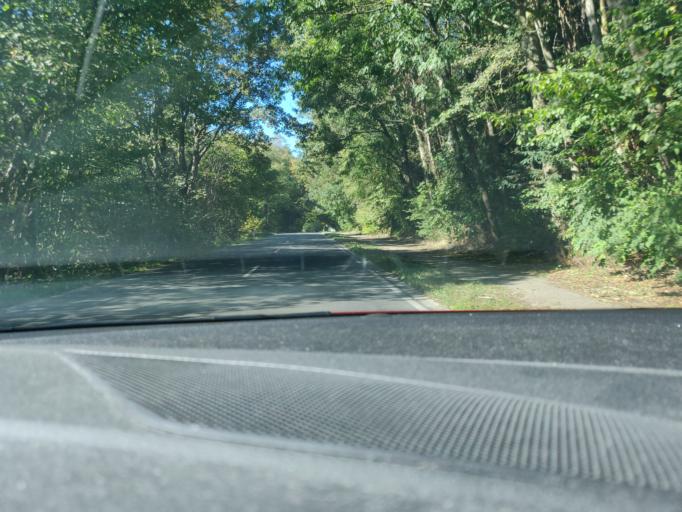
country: DE
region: North Rhine-Westphalia
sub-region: Regierungsbezirk Dusseldorf
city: Heiligenhaus
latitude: 51.3506
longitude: 6.9485
